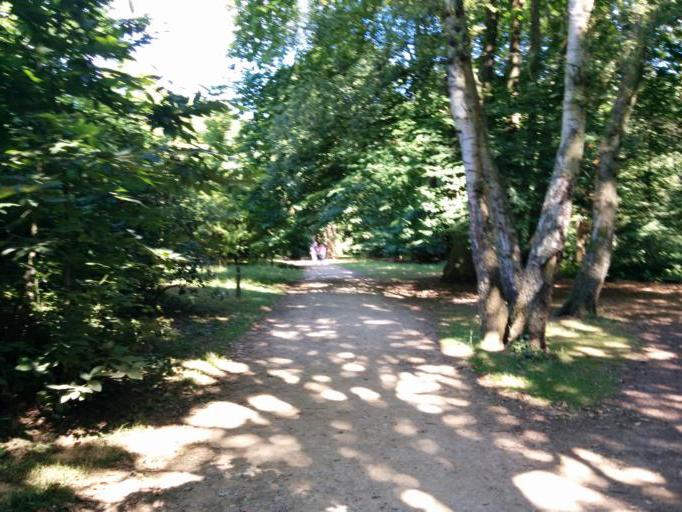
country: GB
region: England
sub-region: Surrey
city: Godalming
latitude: 51.1620
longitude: -0.5842
